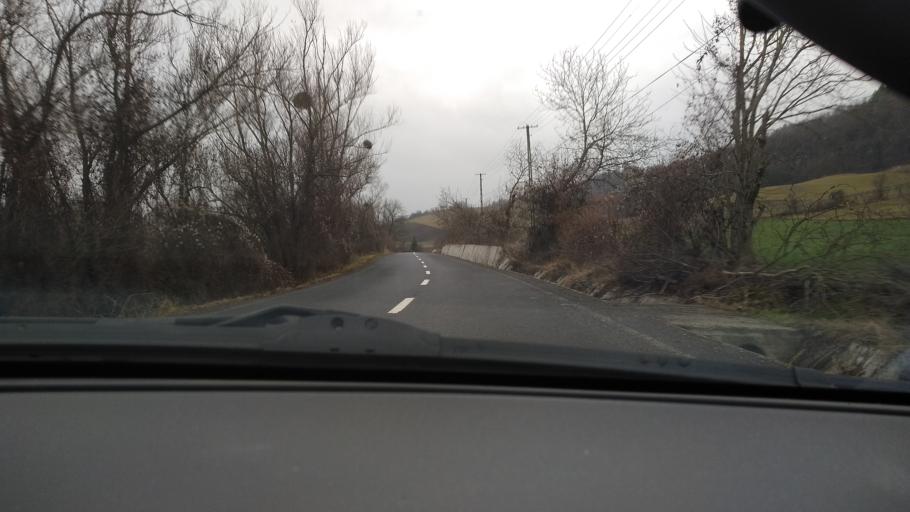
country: RO
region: Mures
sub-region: Comuna Magherani
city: Magherani
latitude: 46.5752
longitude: 24.9280
